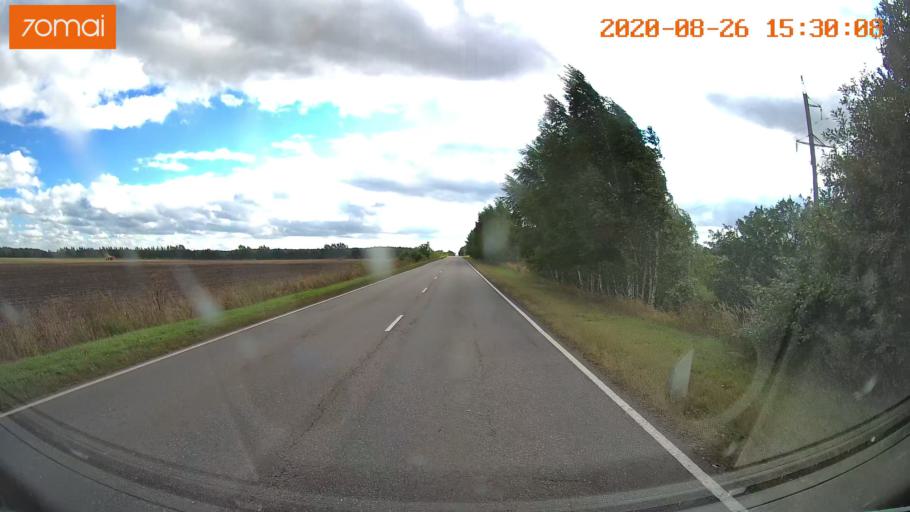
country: RU
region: Tula
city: Severo-Zadonsk
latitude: 54.0943
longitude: 38.3997
